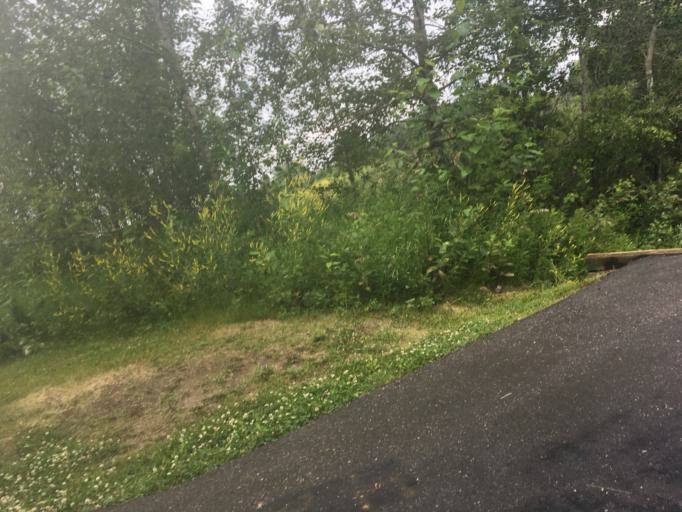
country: CA
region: Alberta
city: Grande Prairie
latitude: 55.1653
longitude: -118.8045
